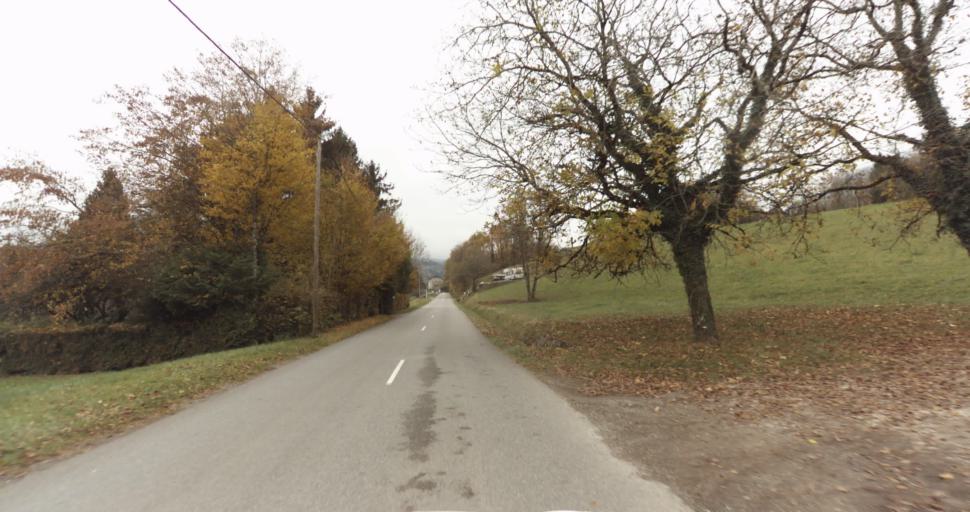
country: FR
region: Rhone-Alpes
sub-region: Departement de la Haute-Savoie
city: Saint-Jorioz
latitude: 45.8389
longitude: 6.1493
